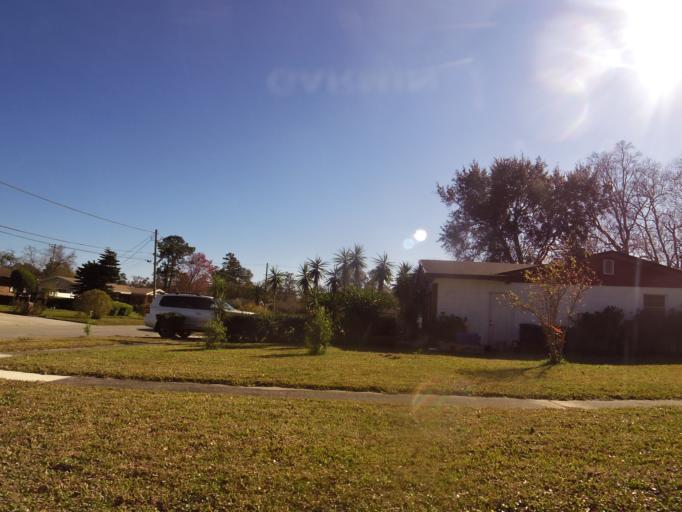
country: US
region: Florida
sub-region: Duval County
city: Jacksonville
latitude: 30.2677
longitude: -81.6035
